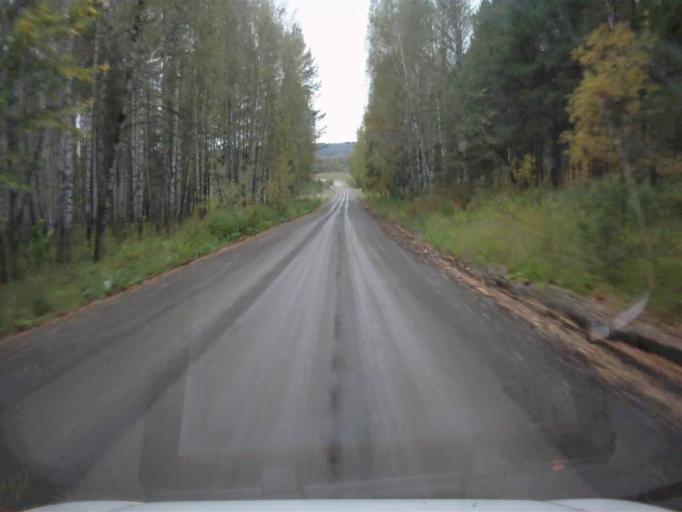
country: RU
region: Chelyabinsk
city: Nyazepetrovsk
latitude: 56.1221
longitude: 59.3609
